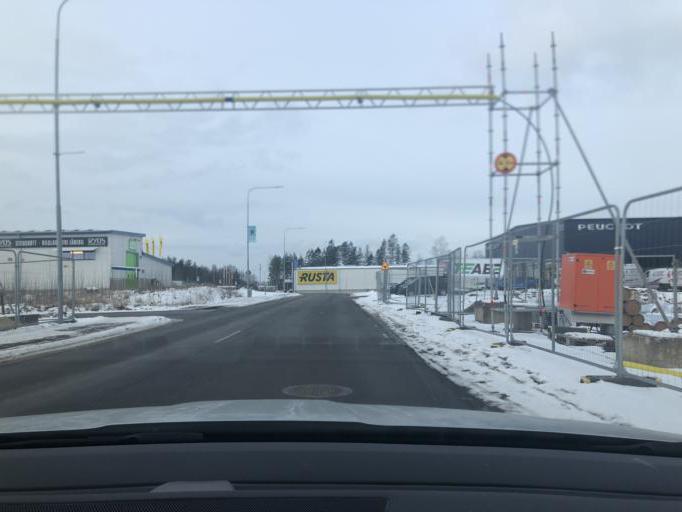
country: SE
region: OEstergoetland
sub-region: Motala Kommun
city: Motala
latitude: 58.5575
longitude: 15.0475
